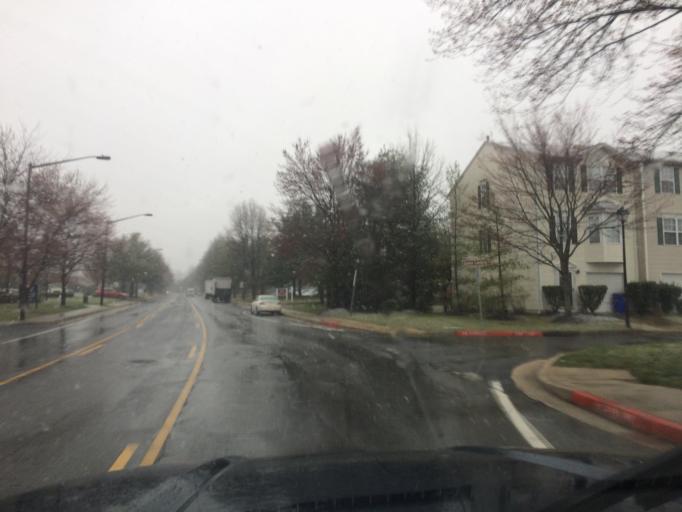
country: US
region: Maryland
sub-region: Howard County
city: Columbia
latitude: 39.2322
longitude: -76.8158
